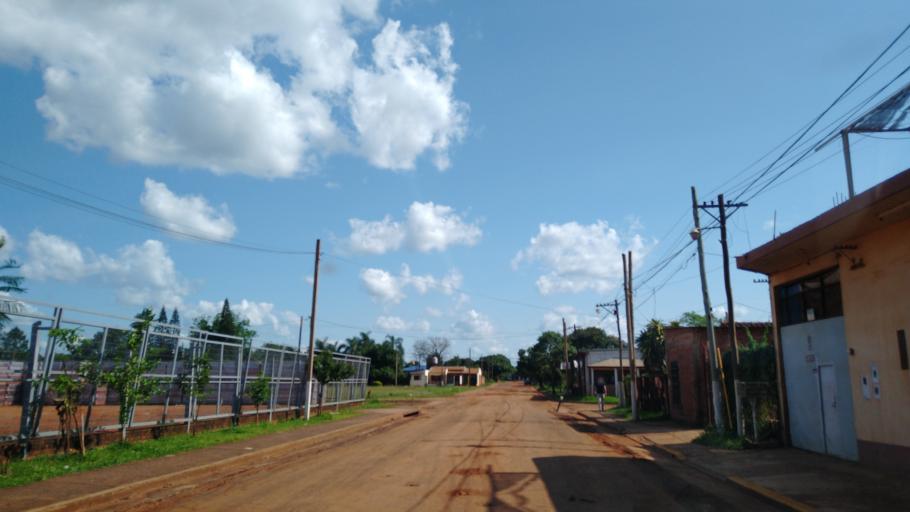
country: AR
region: Misiones
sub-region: Departamento de Capital
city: Posadas
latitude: -27.4033
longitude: -55.9170
